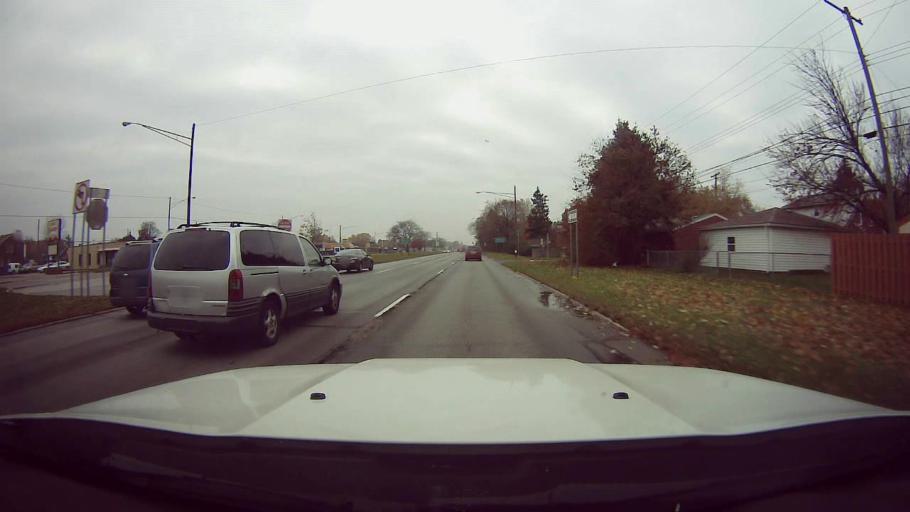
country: US
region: Michigan
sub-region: Wayne County
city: Dearborn Heights
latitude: 42.3221
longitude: -83.2727
